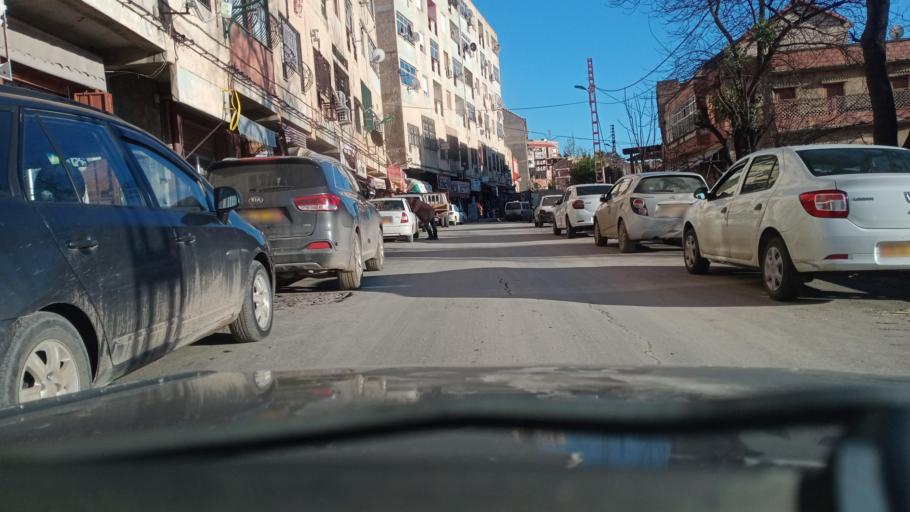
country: DZ
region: Tizi Ouzou
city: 'Ain el Hammam
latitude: 36.5744
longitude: 4.3055
